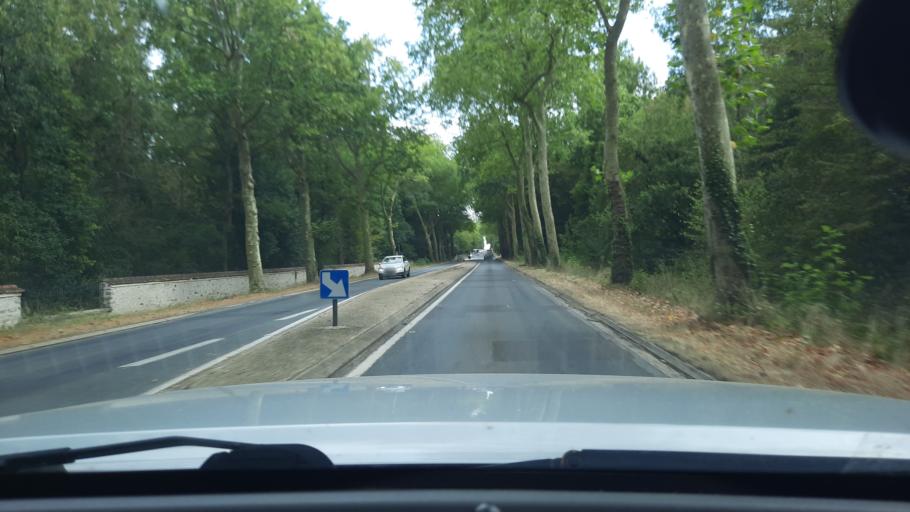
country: FR
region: Ile-de-France
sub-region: Departement de Seine-et-Marne
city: Dammarie-les-Lys
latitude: 48.5143
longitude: 2.6561
